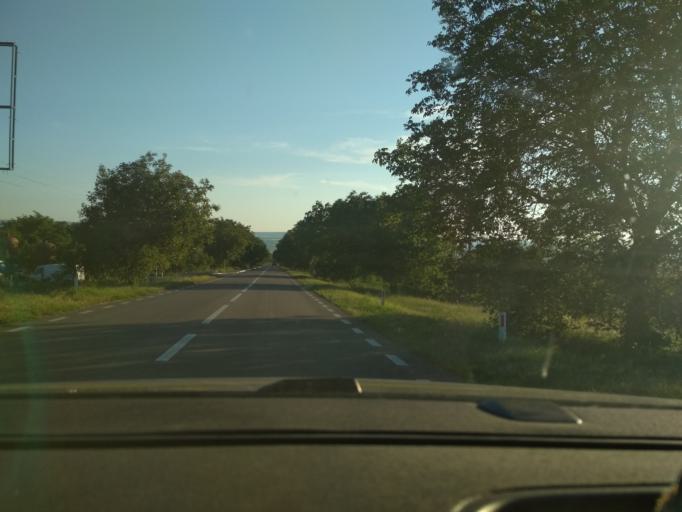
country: RO
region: Iasi
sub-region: Comuna Gorban
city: Gorban
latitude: 46.9475
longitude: 28.1483
